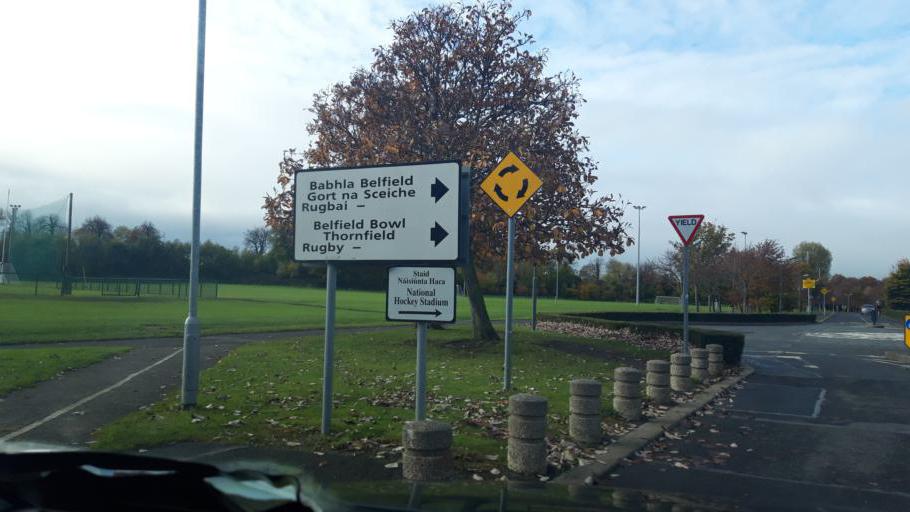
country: IE
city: Clonskeagh
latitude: 53.3079
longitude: -6.2298
